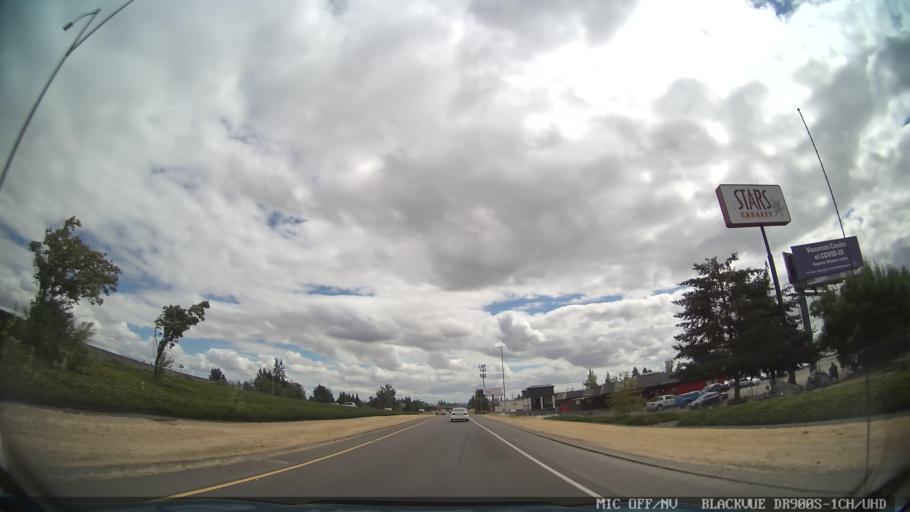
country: US
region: Oregon
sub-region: Marion County
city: Four Corners
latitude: 44.9485
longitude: -122.9908
